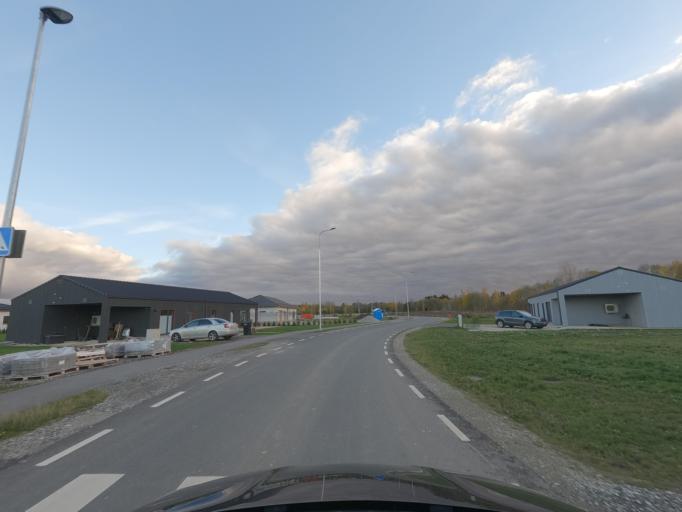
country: EE
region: Harju
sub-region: Saue vald
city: Laagri
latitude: 59.3621
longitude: 24.5725
